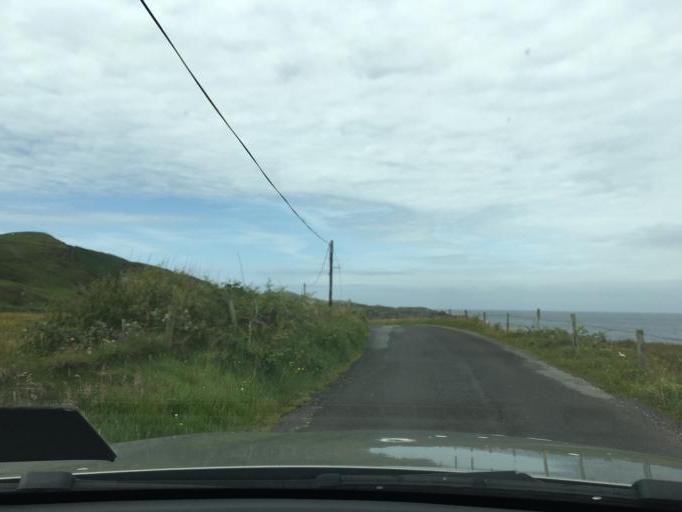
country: IE
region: Ulster
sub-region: County Donegal
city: Carndonagh
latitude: 55.3737
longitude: -7.3442
